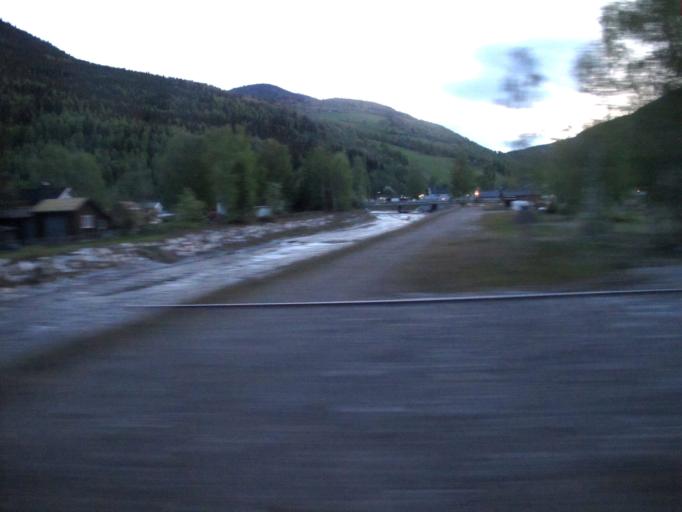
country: NO
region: Oppland
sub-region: Nord-Fron
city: Vinstra
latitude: 61.6629
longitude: 9.6783
